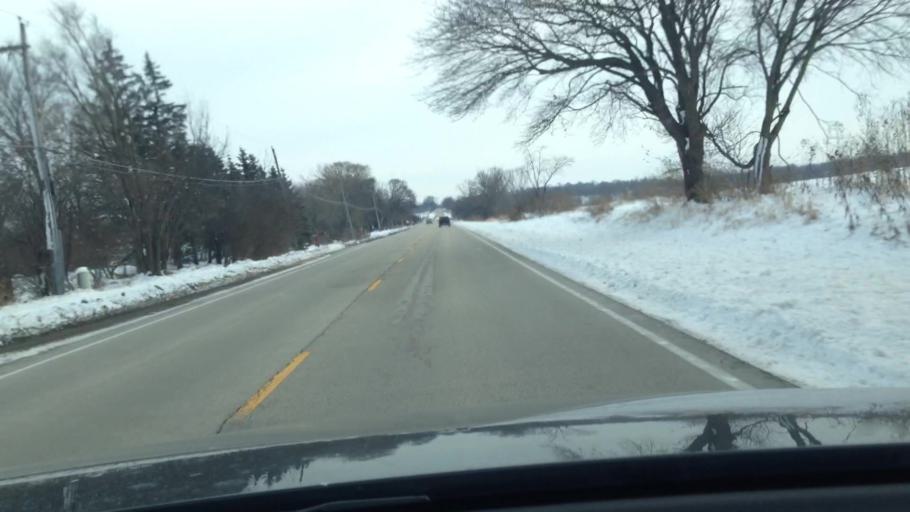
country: US
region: Illinois
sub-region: McHenry County
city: Woodstock
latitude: 42.3749
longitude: -88.4432
